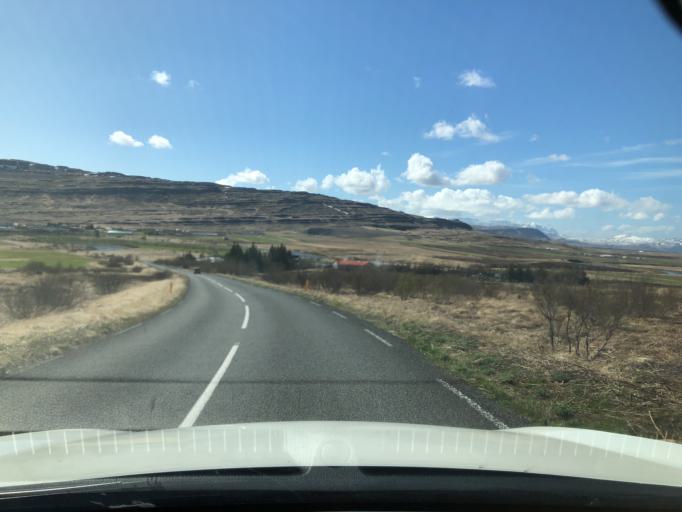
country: IS
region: West
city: Borgarnes
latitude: 64.6675
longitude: -21.4078
